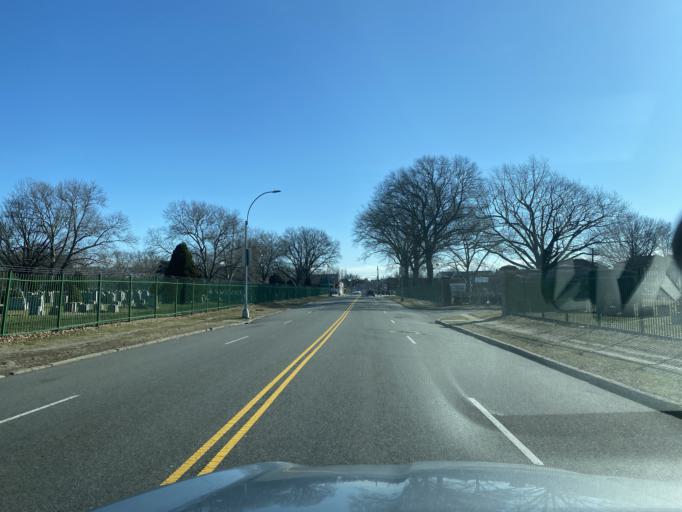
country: US
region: New York
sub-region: Queens County
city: Borough of Queens
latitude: 40.7125
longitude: -73.8641
